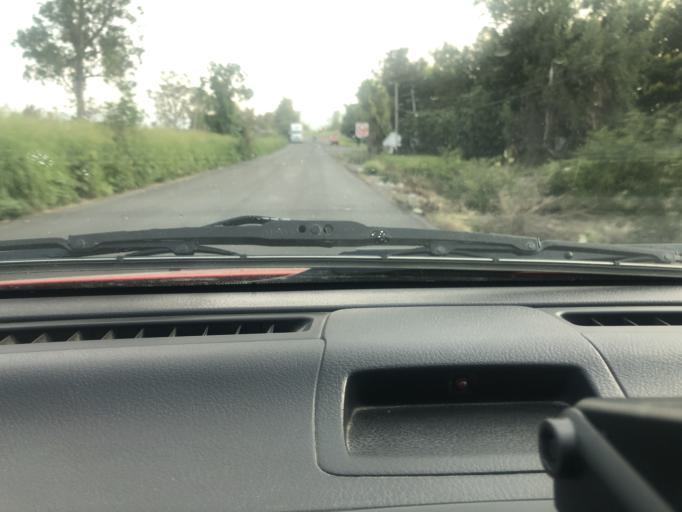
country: MX
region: Jalisco
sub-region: San Pedro Tlaquepaque
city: Paseo del Prado
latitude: 20.5701
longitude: -103.4071
